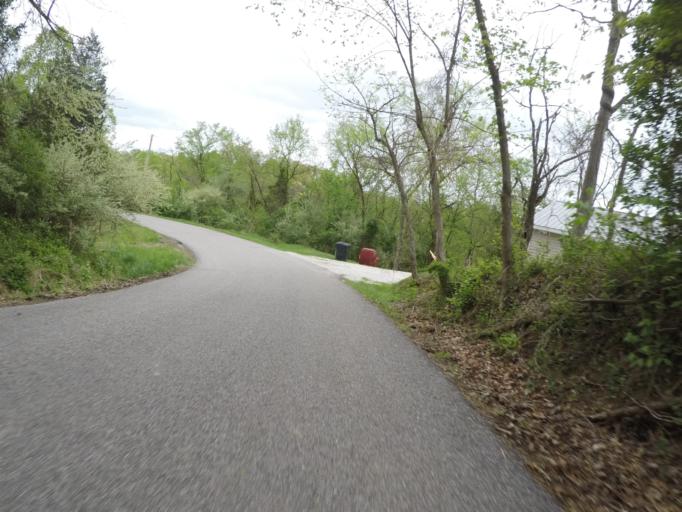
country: US
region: West Virginia
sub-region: Cabell County
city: Barboursville
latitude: 38.3962
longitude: -82.2550
